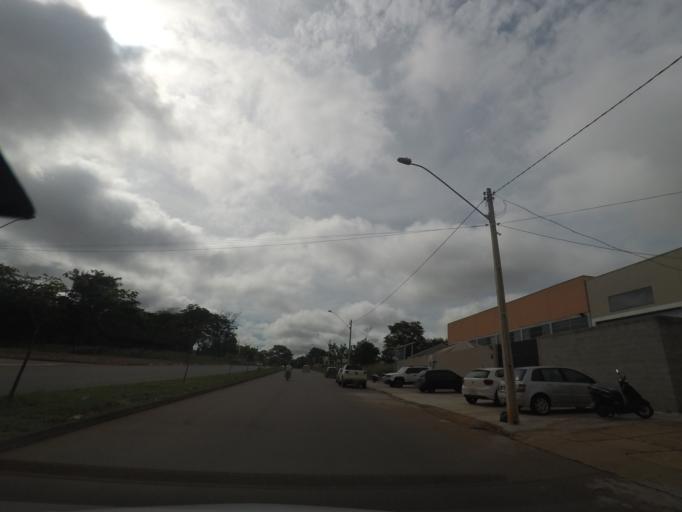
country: BR
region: Goias
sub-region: Goiania
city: Goiania
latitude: -16.7425
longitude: -49.3142
